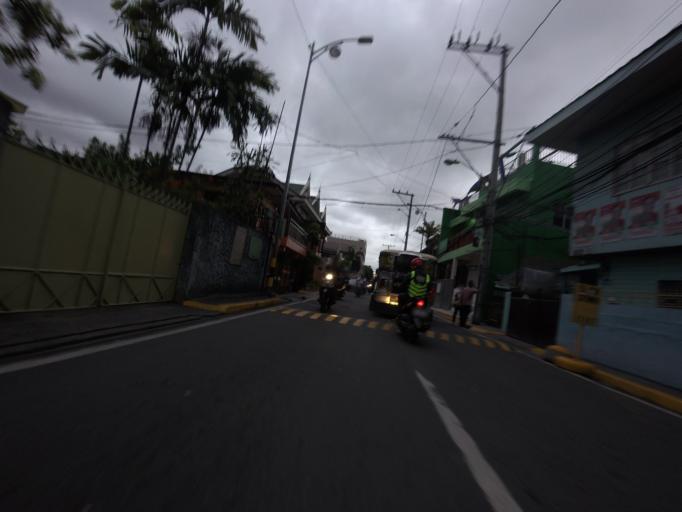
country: PH
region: Metro Manila
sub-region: San Juan
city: San Juan
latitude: 14.5876
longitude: 121.0163
